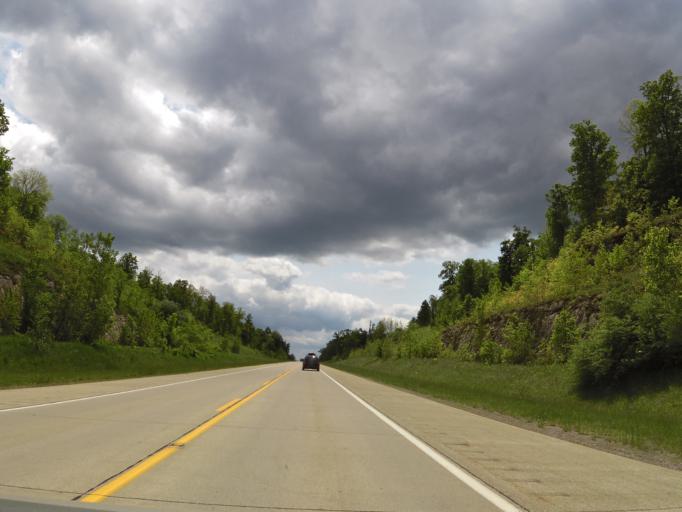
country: US
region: Ohio
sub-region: Meigs County
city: Pomeroy
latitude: 39.1666
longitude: -82.0397
